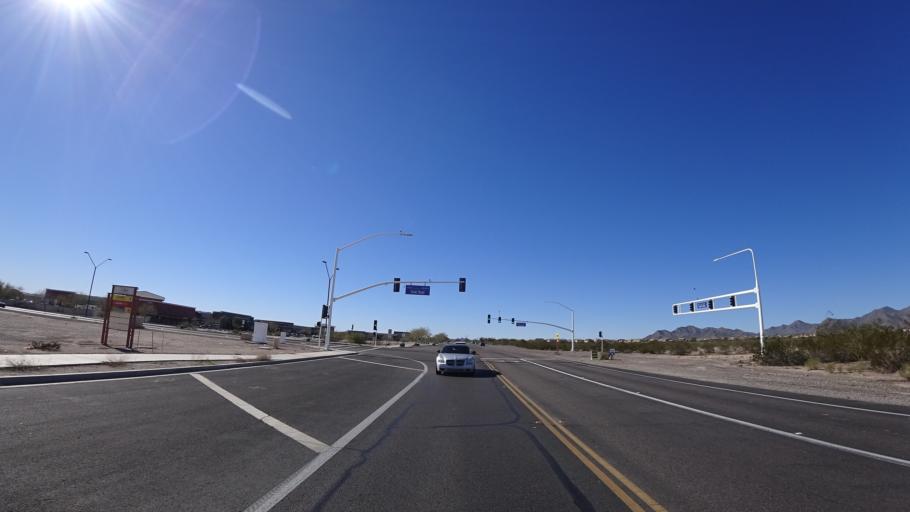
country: US
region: Arizona
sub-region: Maricopa County
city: Buckeye
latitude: 33.4356
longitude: -112.5155
